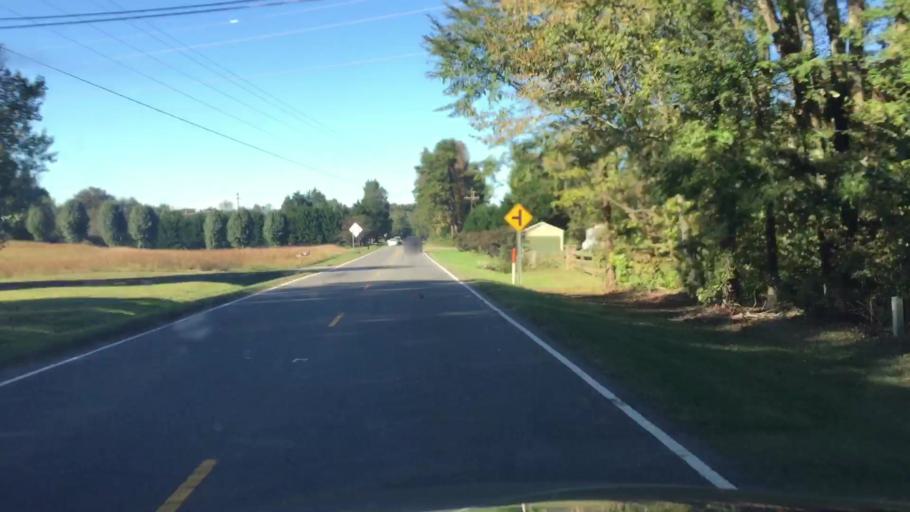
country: US
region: North Carolina
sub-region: Gaston County
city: Davidson
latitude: 35.5167
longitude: -80.7700
